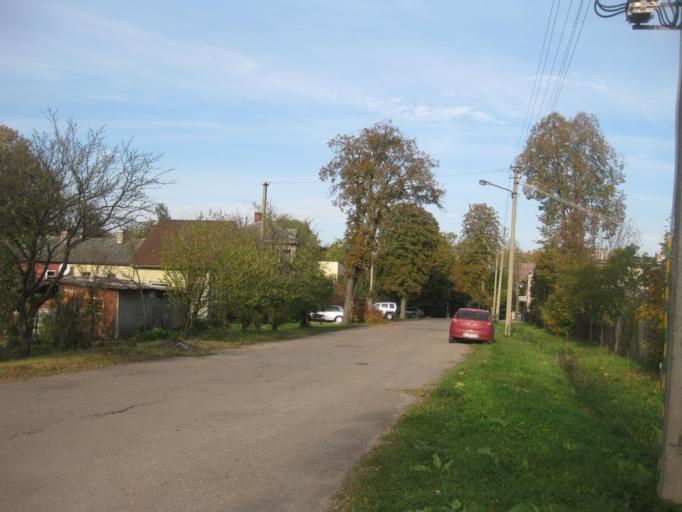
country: LT
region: Kauno apskritis
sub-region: Kaunas
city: Kaunas
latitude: 54.8927
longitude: 23.8750
